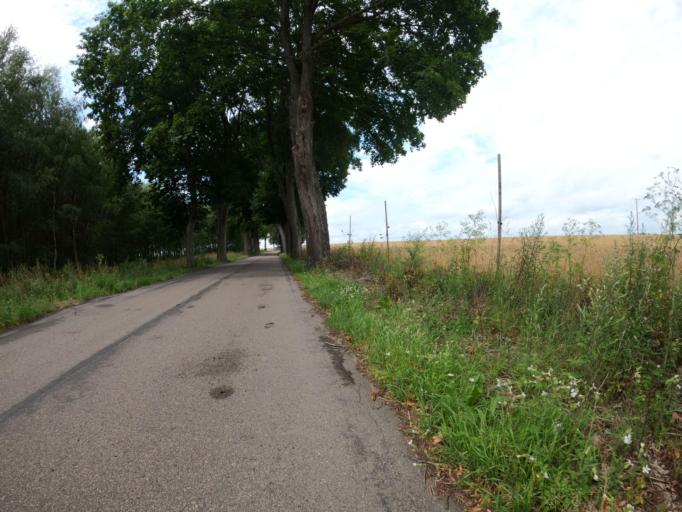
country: PL
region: West Pomeranian Voivodeship
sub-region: Powiat szczecinecki
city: Grzmiaca
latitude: 53.7862
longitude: 16.4894
